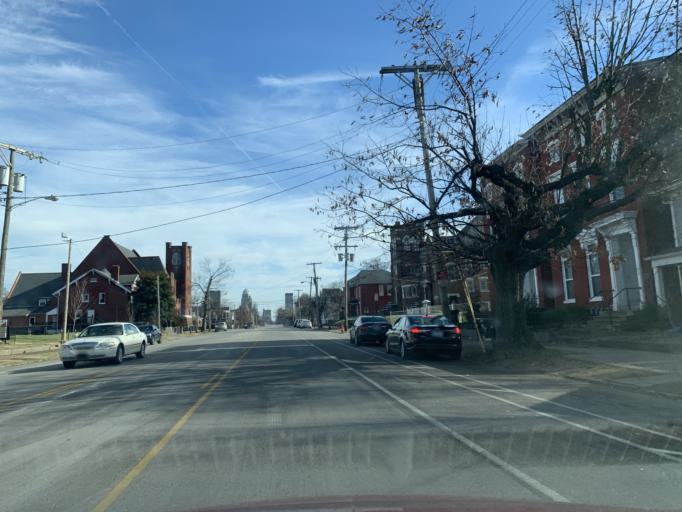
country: US
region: Kentucky
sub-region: Jefferson County
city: Louisville
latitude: 38.2568
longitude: -85.7835
